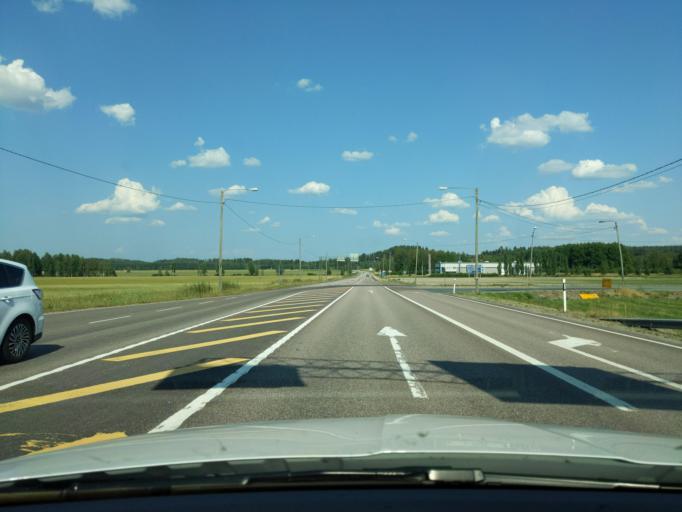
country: FI
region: Haeme
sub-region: Riihimaeki
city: Oitti
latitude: 60.7941
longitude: 25.0126
